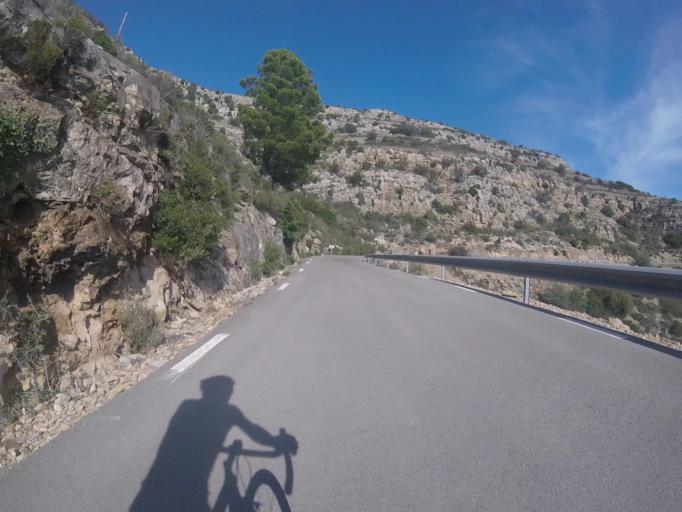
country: ES
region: Valencia
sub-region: Provincia de Castello
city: Sarratella
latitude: 40.2837
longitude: 0.0369
